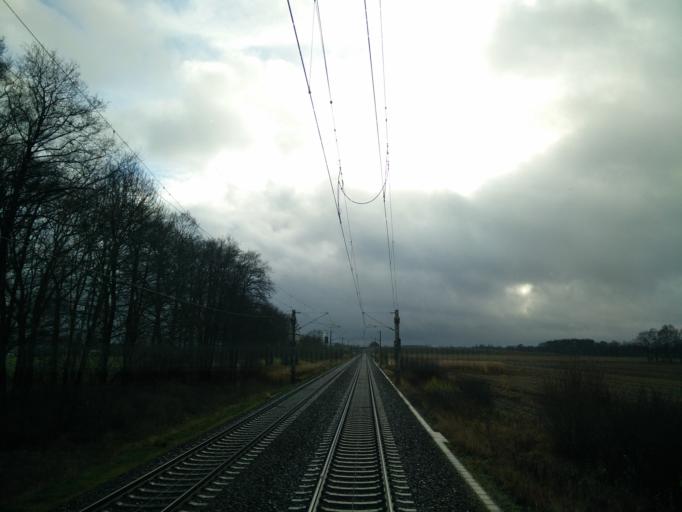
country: DE
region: Brandenburg
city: Karstadt
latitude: 53.1797
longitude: 11.7356
